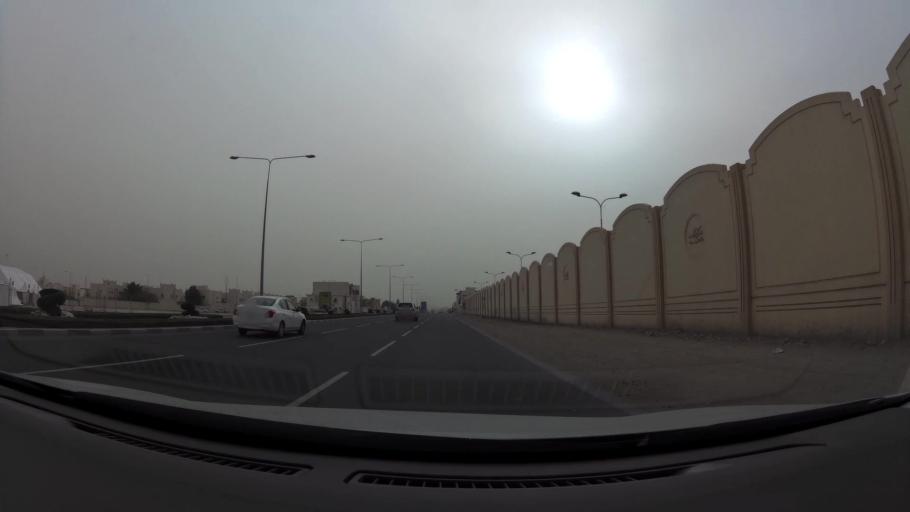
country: QA
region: Baladiyat ad Dawhah
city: Doha
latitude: 25.2547
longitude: 51.4920
